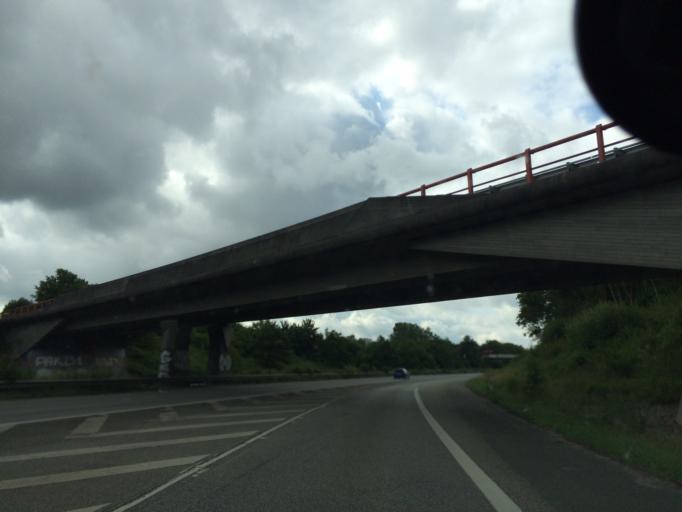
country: DE
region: Schleswig-Holstein
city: Kiel
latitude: 54.3484
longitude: 10.1200
